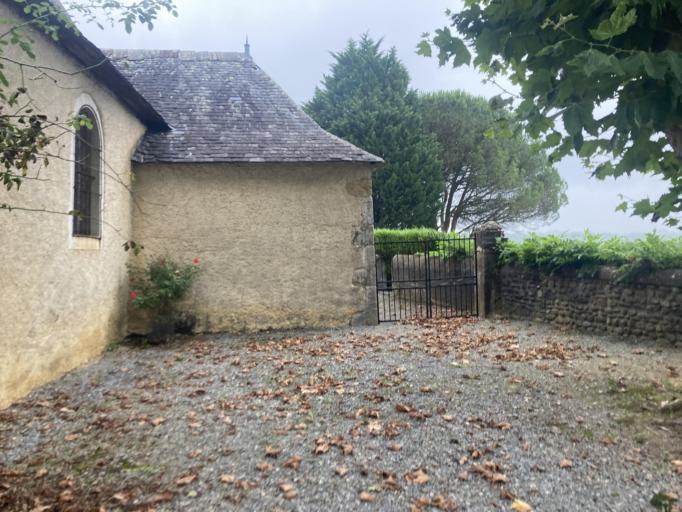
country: FR
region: Aquitaine
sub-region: Departement des Pyrenees-Atlantiques
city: Ledeuix
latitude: 43.2353
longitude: -0.5725
